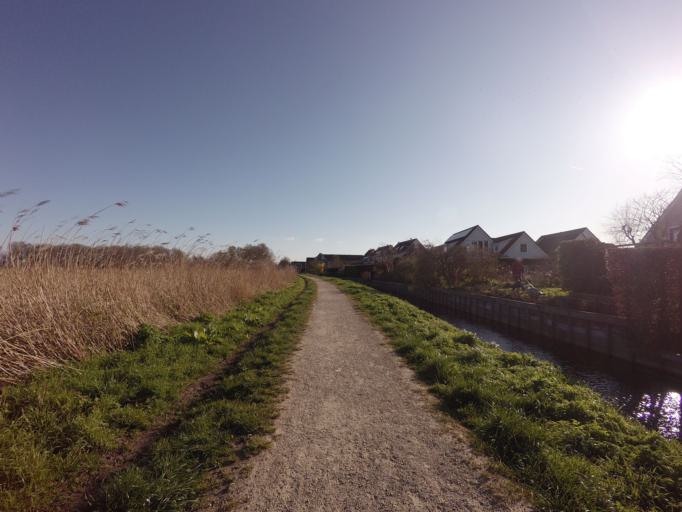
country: NL
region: Utrecht
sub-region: Stichtse Vecht
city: Vreeland
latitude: 52.2590
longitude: 5.0483
